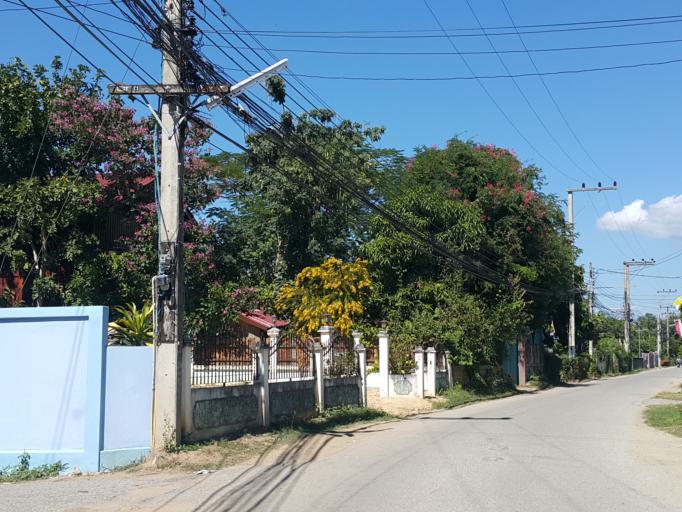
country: TH
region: Chiang Mai
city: San Sai
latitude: 18.8137
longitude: 99.0587
